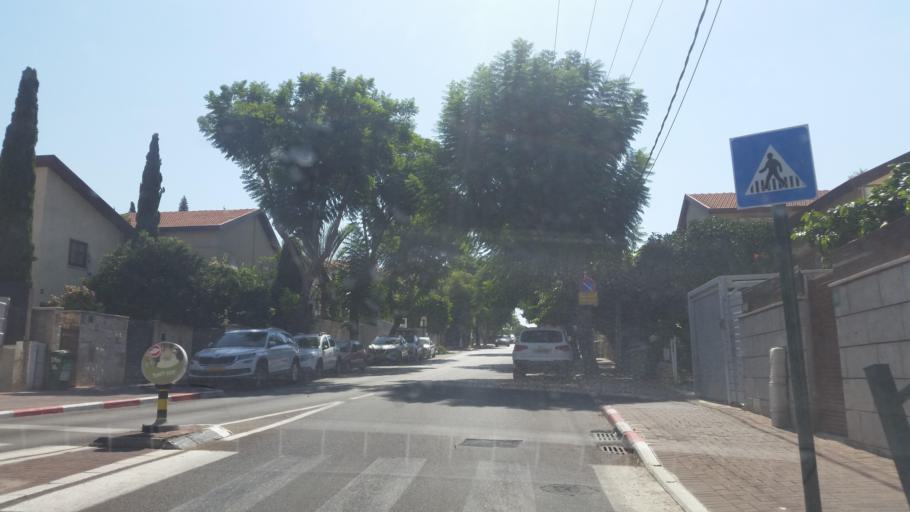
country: IL
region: Central District
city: Ra'anana
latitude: 32.1814
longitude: 34.8853
